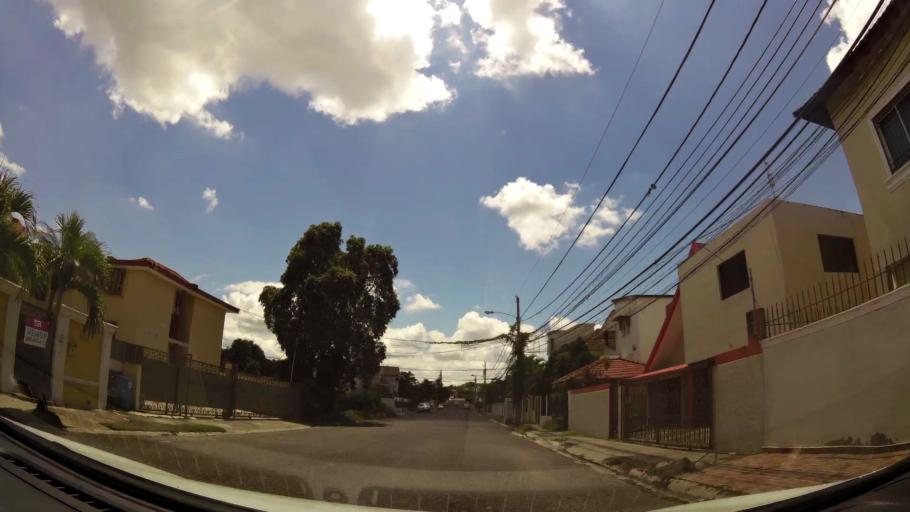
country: DO
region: Santiago
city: Santiago de los Caballeros
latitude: 19.4742
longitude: -70.6737
